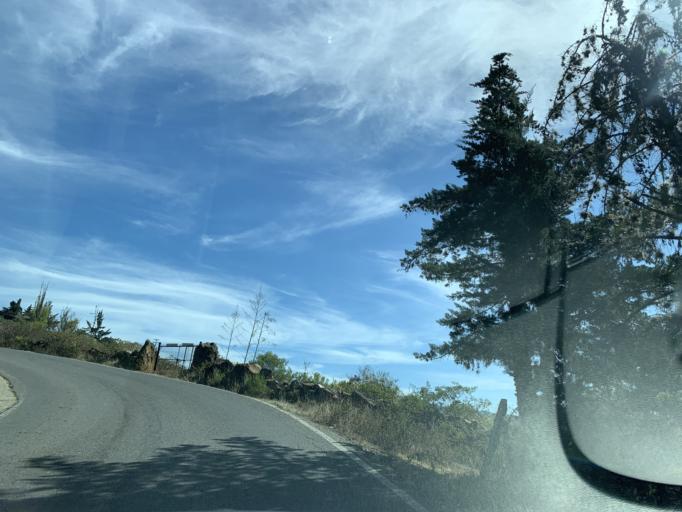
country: CO
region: Boyaca
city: Santa Sofia
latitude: 5.6880
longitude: -73.5882
